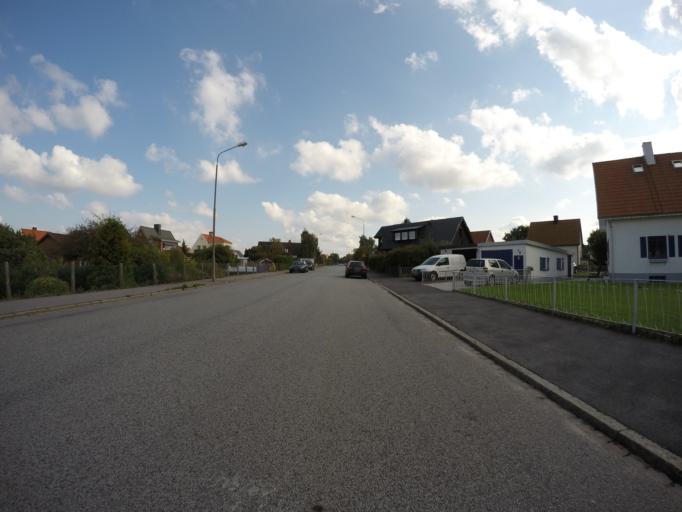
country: SE
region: Skane
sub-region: Burlovs Kommun
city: Arloev
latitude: 55.5898
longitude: 13.0753
